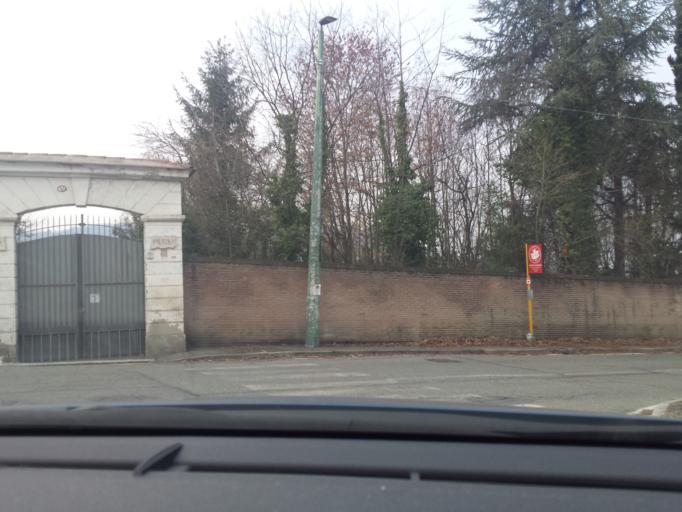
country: IT
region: Piedmont
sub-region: Provincia di Torino
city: Turin
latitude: 45.0526
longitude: 7.7182
